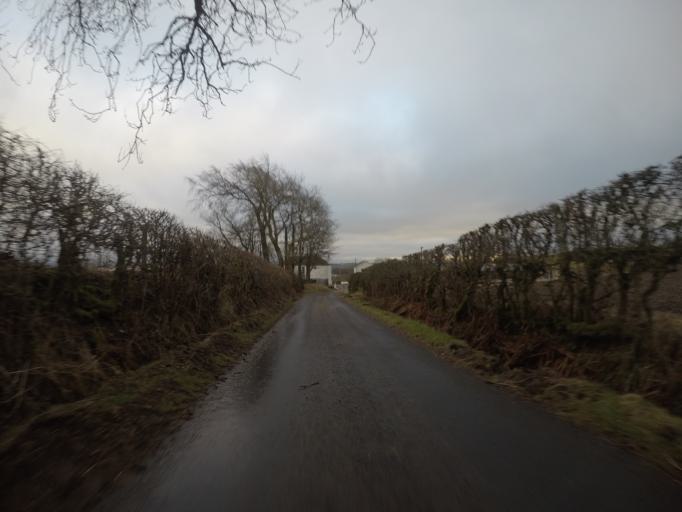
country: GB
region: Scotland
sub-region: North Ayrshire
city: Dalry
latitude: 55.7205
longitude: -4.7601
